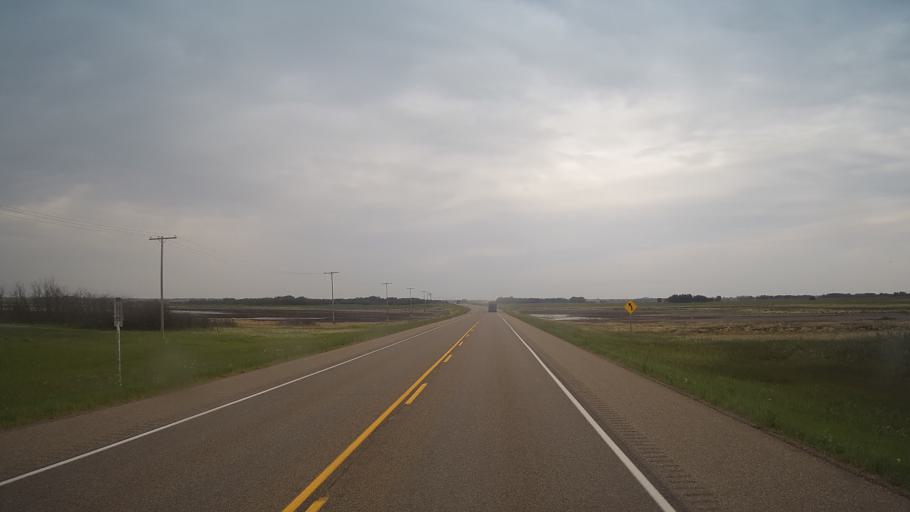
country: CA
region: Saskatchewan
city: Langham
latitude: 52.1294
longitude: -107.0999
